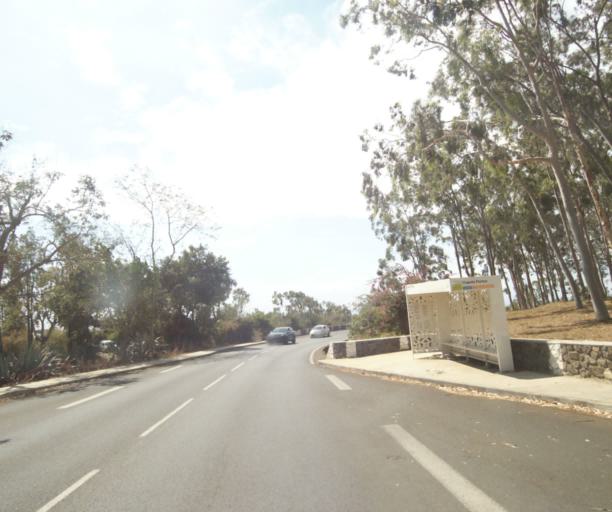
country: RE
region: Reunion
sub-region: Reunion
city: Saint-Paul
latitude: -21.0560
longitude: 55.2654
